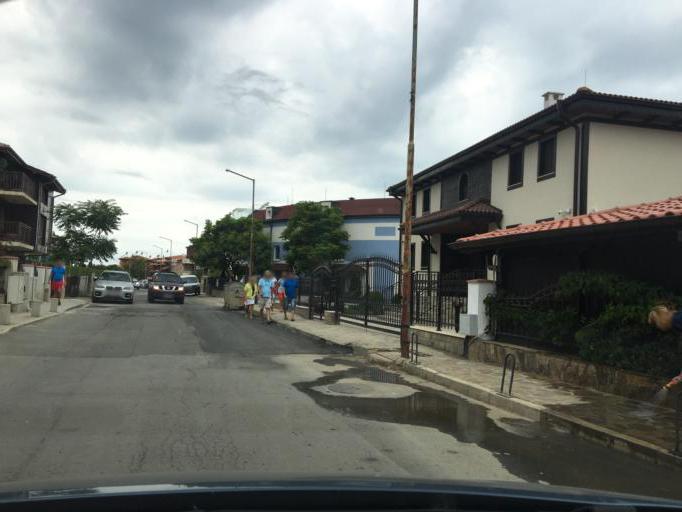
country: BG
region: Burgas
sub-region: Obshtina Sozopol
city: Sozopol
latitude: 42.4067
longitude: 27.7101
